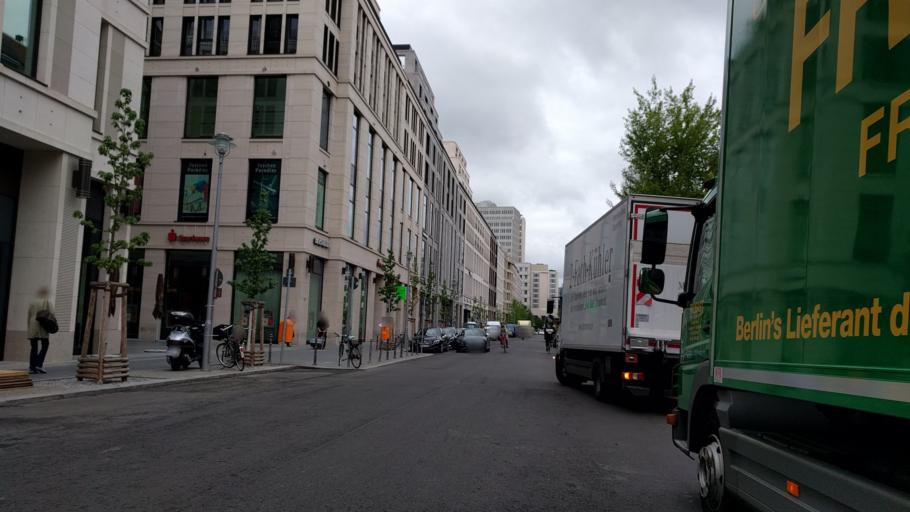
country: DE
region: Berlin
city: Tiergarten Bezirk
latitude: 52.5111
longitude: 13.3815
